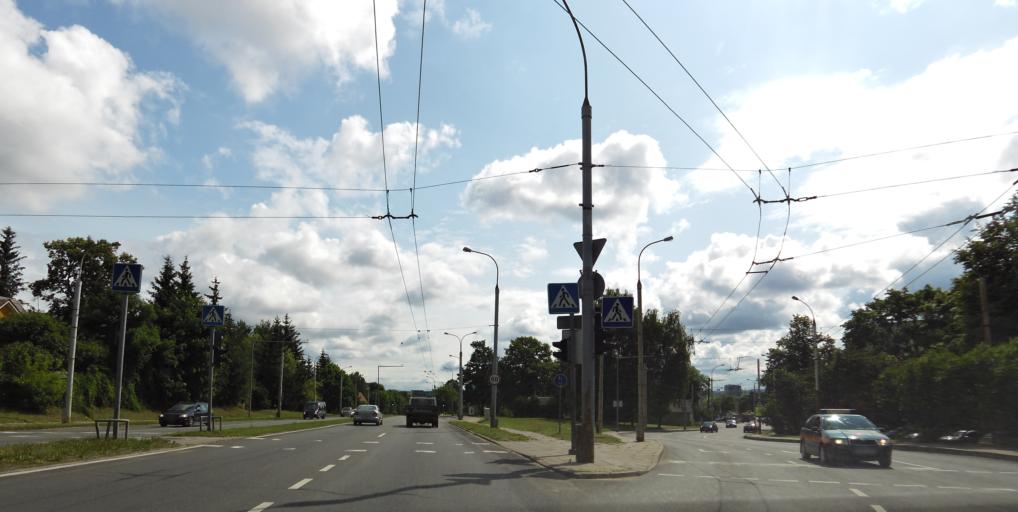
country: LT
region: Vilnius County
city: Seskine
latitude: 54.6993
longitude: 25.2434
